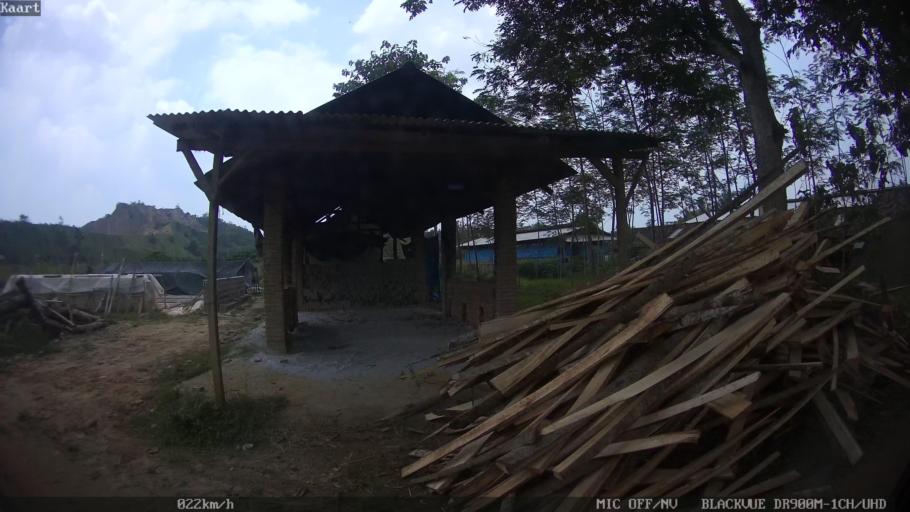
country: ID
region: Lampung
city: Gadingrejo
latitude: -5.3881
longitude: 105.0356
